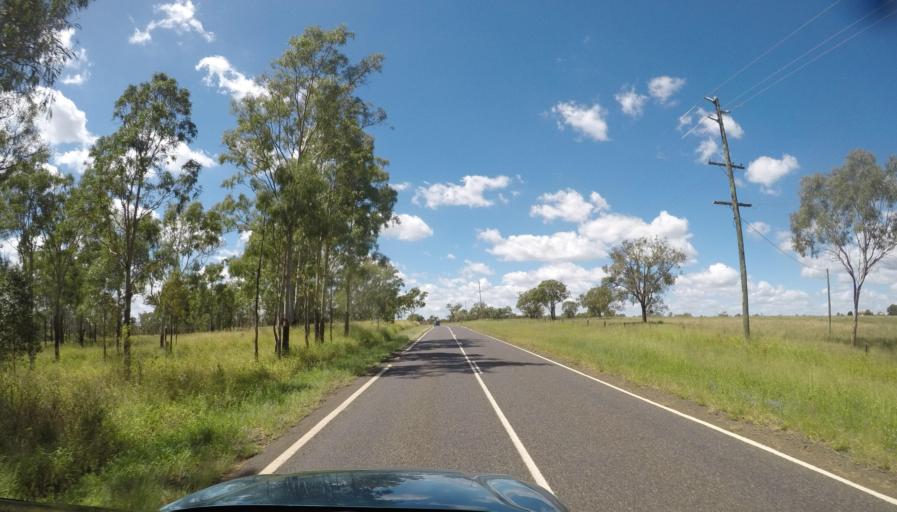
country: AU
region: Queensland
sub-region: Toowoomba
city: Oakey
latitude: -27.5548
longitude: 151.7032
